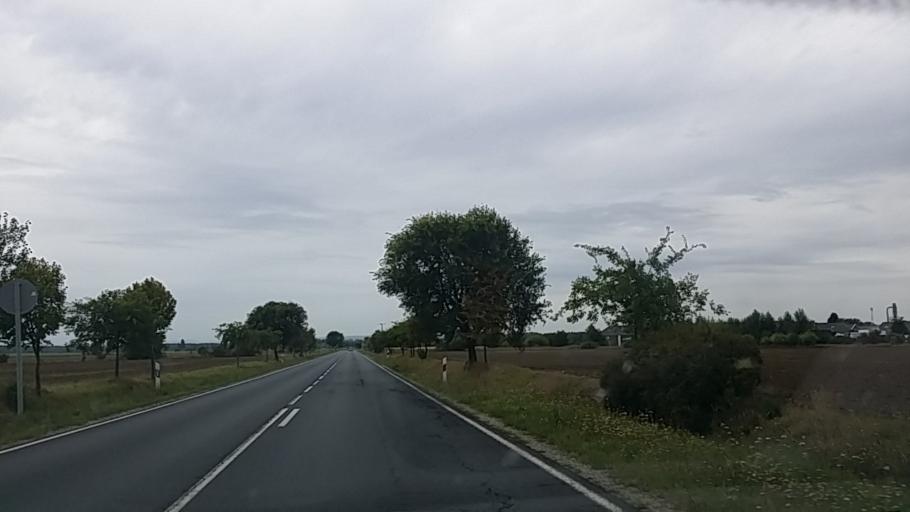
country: HU
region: Gyor-Moson-Sopron
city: Fertoszentmiklos
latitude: 47.5888
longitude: 16.8599
